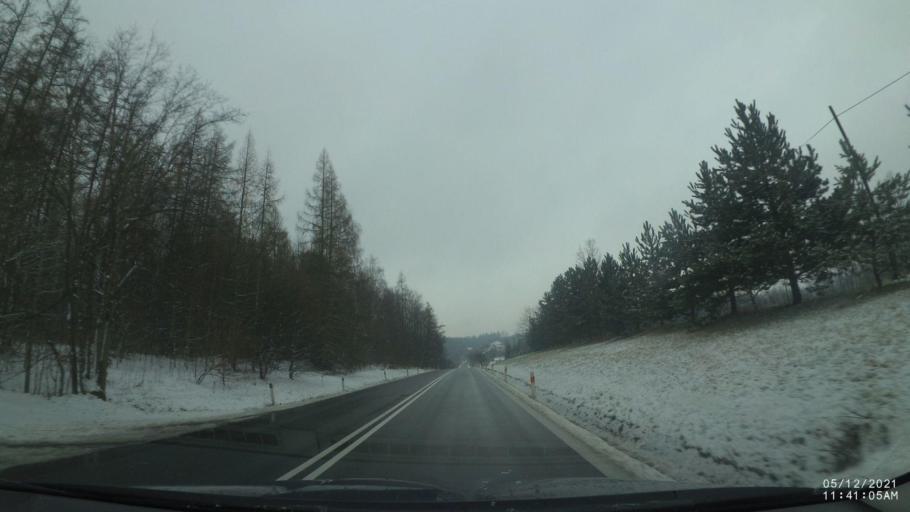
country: CZ
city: Dobruska
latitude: 50.2660
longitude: 16.1966
